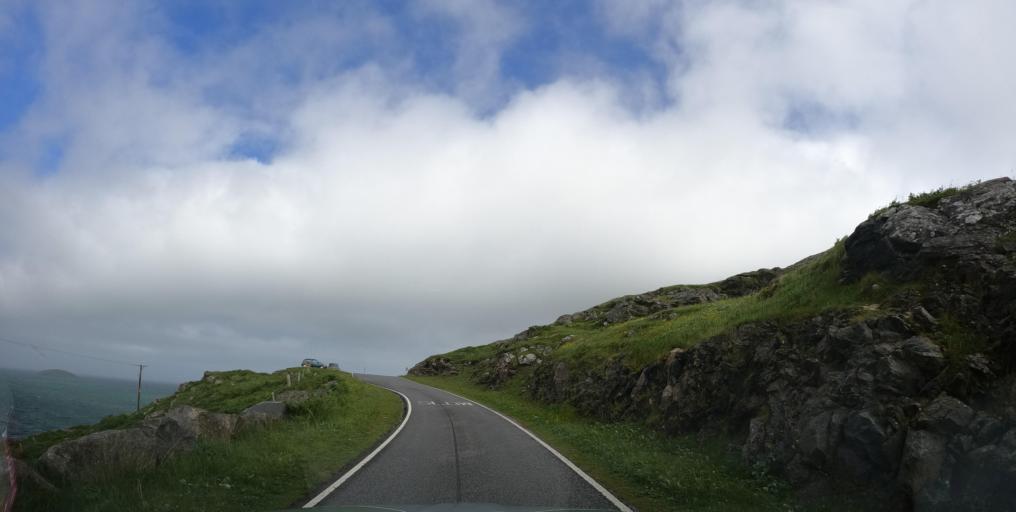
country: GB
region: Scotland
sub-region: Eilean Siar
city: Isle of South Uist
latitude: 57.0750
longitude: -7.3021
